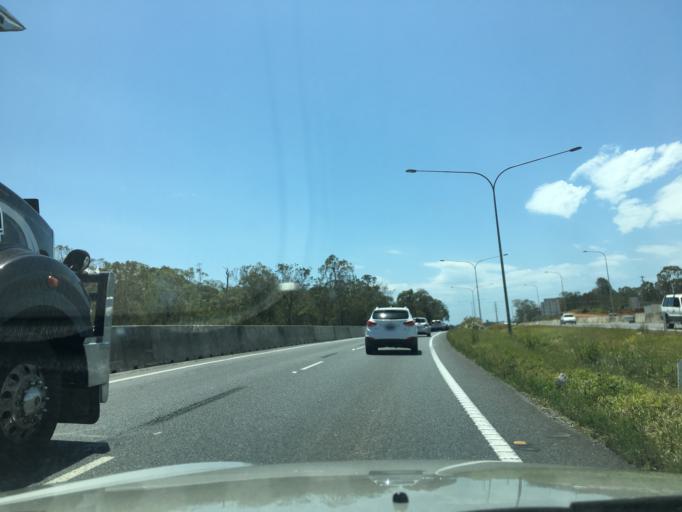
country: AU
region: Queensland
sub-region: Brisbane
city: Shorncliffe
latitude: -27.3719
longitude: 153.0965
